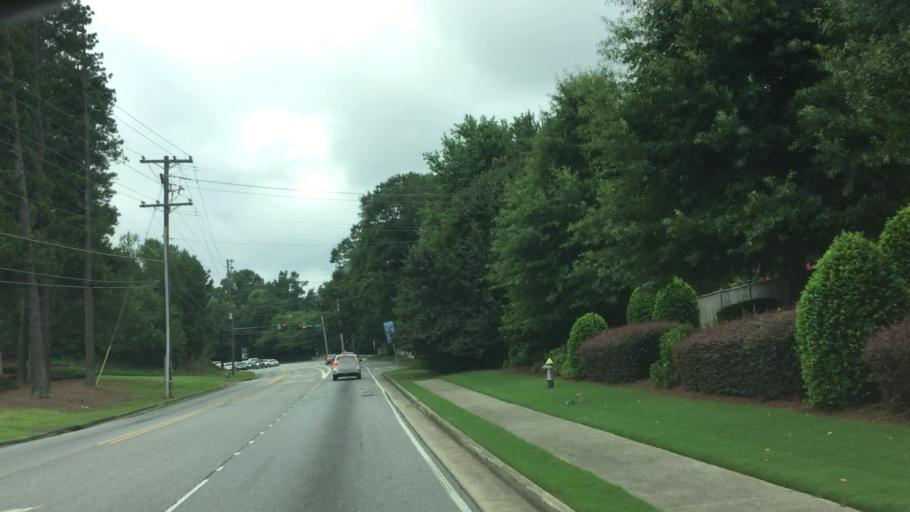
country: US
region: Georgia
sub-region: Fulton County
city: Johns Creek
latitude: 34.0955
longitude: -84.2106
